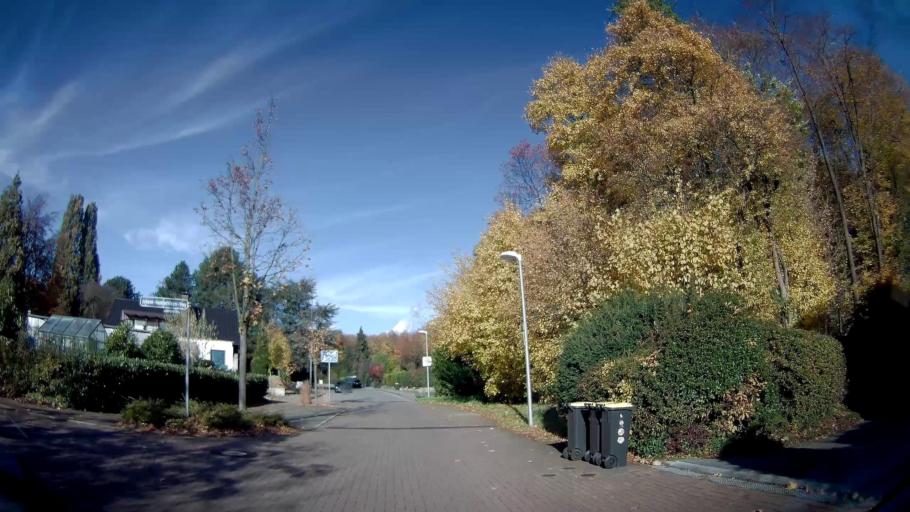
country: DE
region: North Rhine-Westphalia
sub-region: Regierungsbezirk Munster
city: Gladbeck
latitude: 51.5766
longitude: 7.0114
